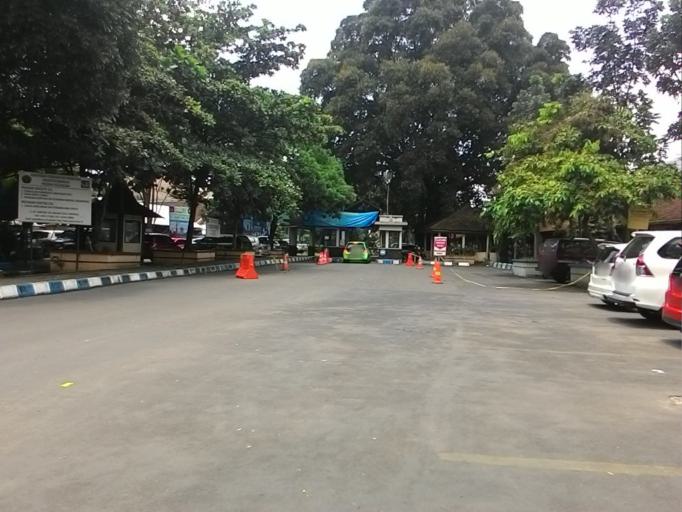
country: ID
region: East Java
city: Malang
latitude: -7.9475
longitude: 112.6130
